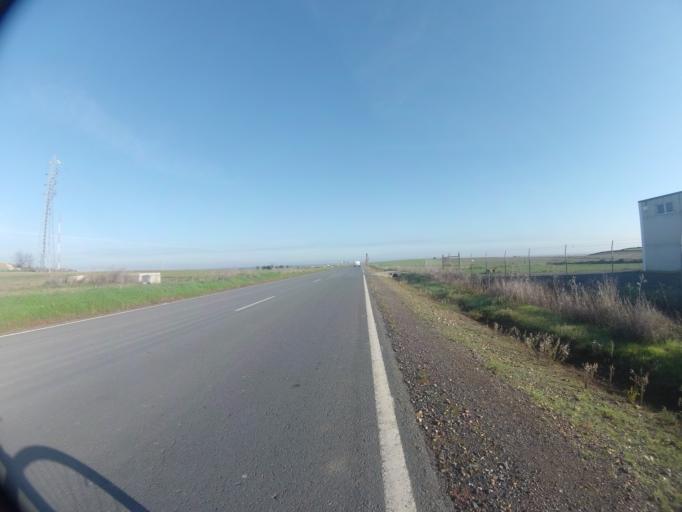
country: ES
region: Andalusia
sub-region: Provincia de Huelva
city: Huelva
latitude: 37.3023
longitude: -6.9251
